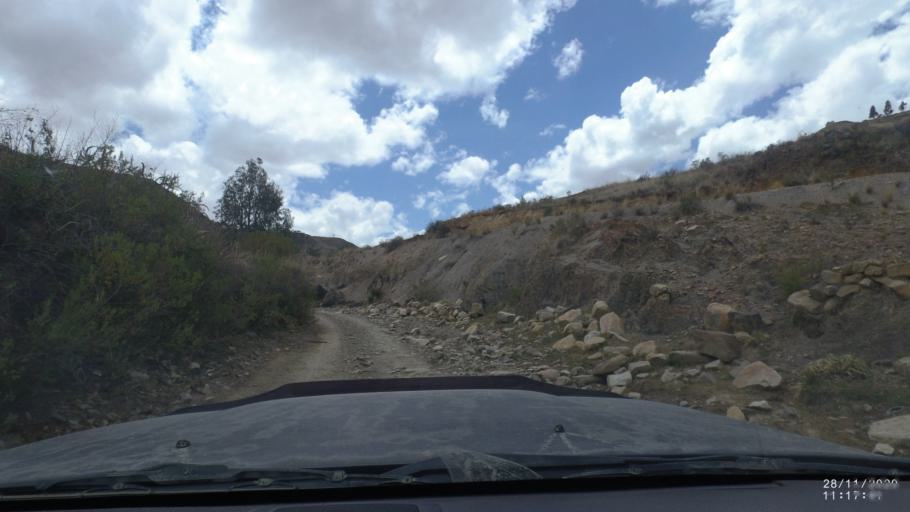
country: BO
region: Cochabamba
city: Tarata
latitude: -17.7533
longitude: -66.0771
